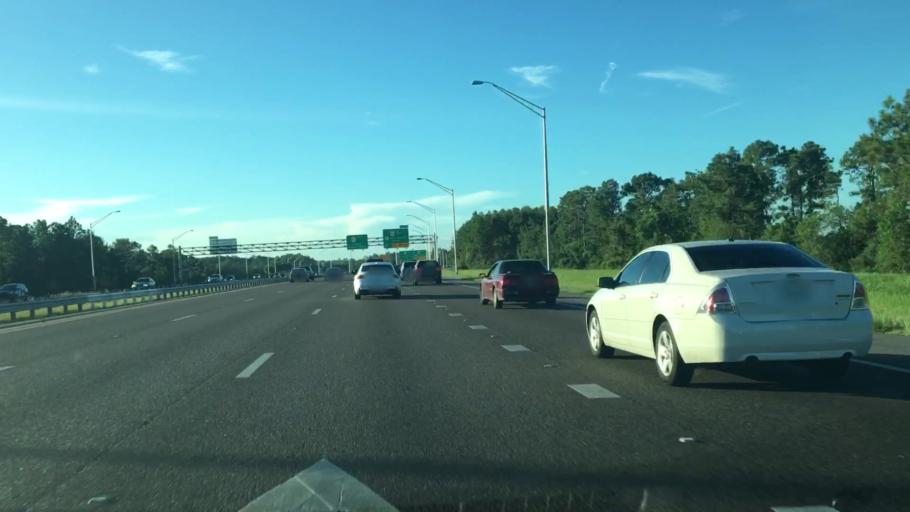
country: US
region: Florida
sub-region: Orange County
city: Azalea Park
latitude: 28.4625
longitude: -81.2338
